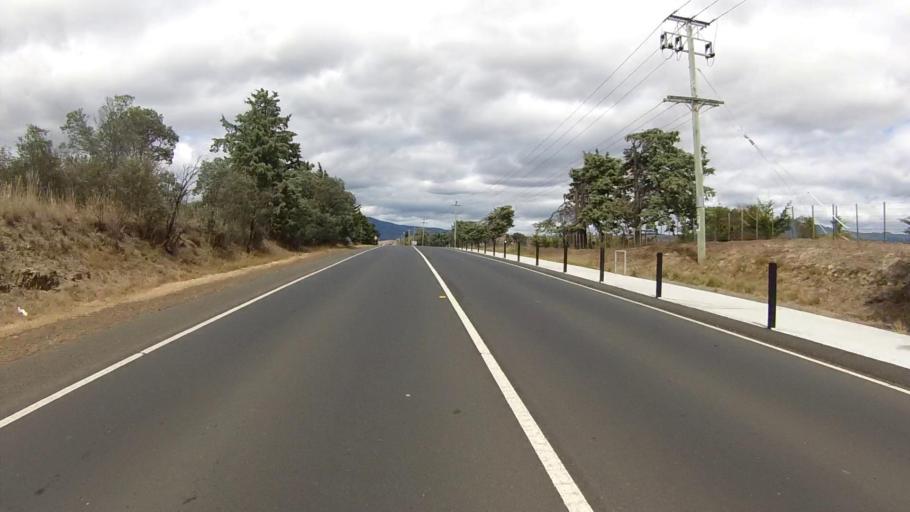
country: AU
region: Tasmania
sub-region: Brighton
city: Bridgewater
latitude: -42.6897
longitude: 147.2608
